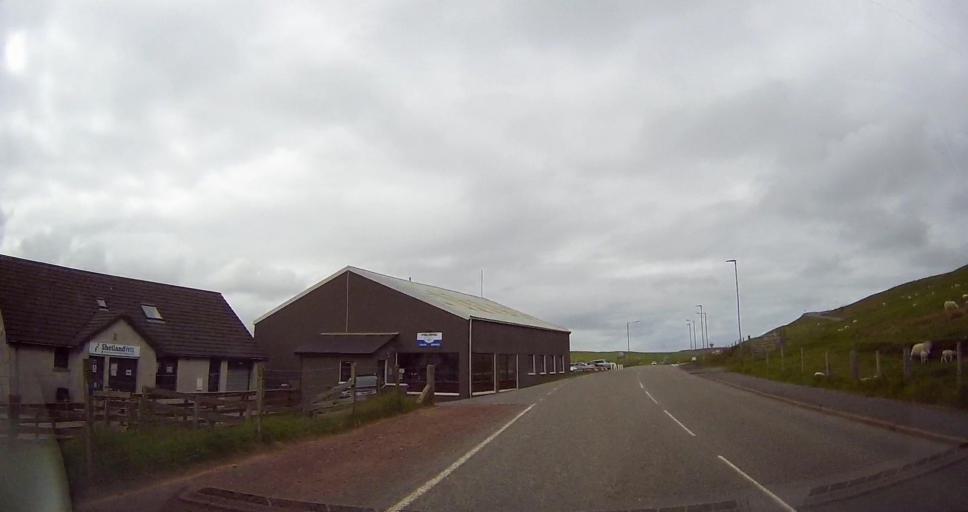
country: GB
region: Scotland
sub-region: Shetland Islands
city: Lerwick
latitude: 60.2532
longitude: -1.4026
